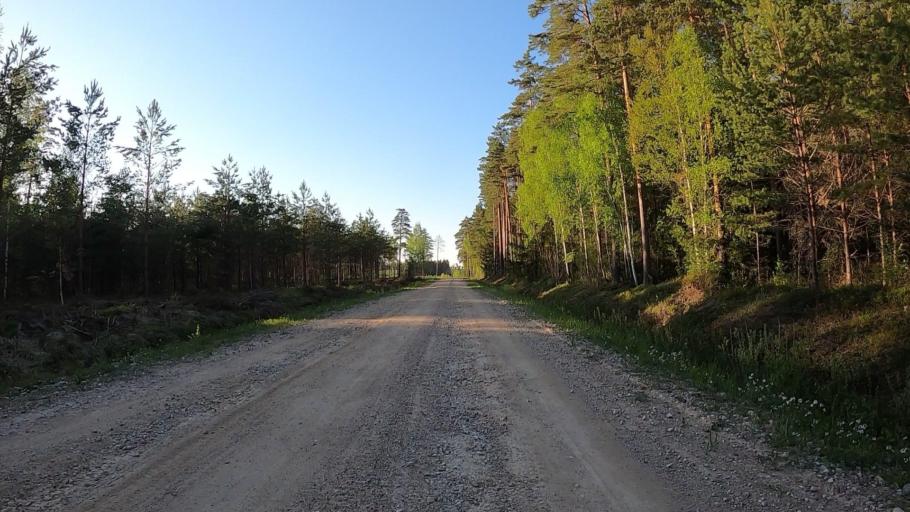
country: LV
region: Kekava
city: Kekava
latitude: 56.7666
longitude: 24.2227
